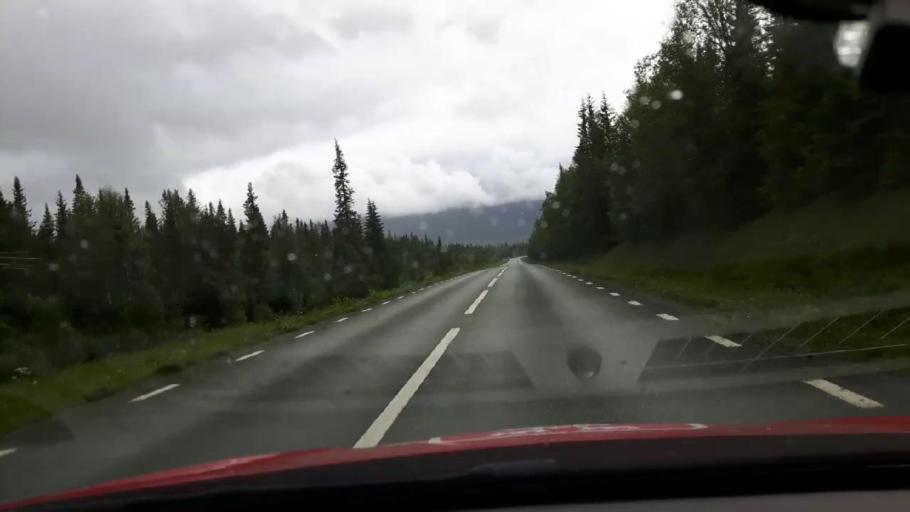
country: NO
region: Nord-Trondelag
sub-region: Meraker
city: Meraker
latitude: 63.2961
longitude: 12.4097
